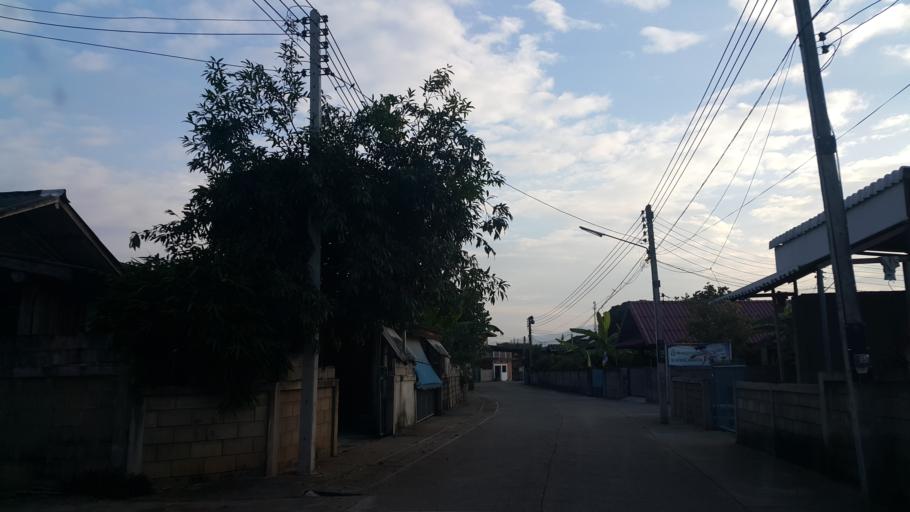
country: TH
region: Lampang
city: Sop Prap
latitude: 17.8896
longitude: 99.3356
